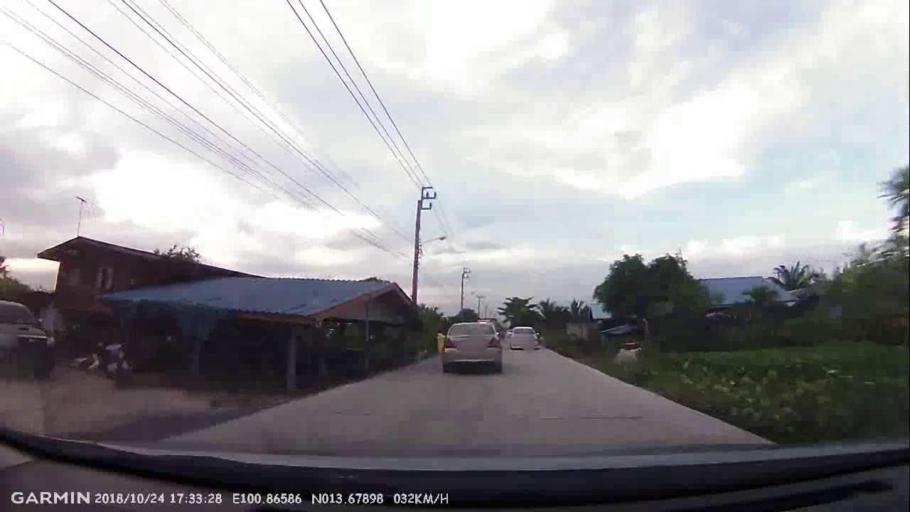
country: TH
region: Samut Prakan
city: Ban Khlong Bang Sao Thong
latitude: 13.6792
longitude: 100.8657
